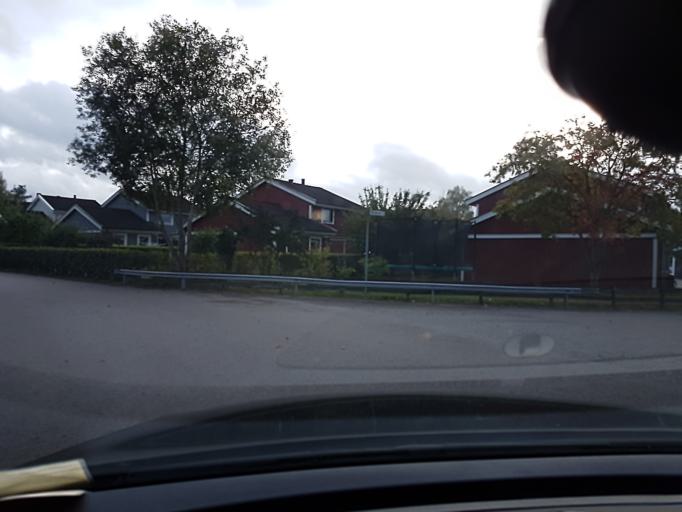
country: SE
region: Kronoberg
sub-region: Vaxjo Kommun
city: Vaexjoe
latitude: 56.8469
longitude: 14.8203
